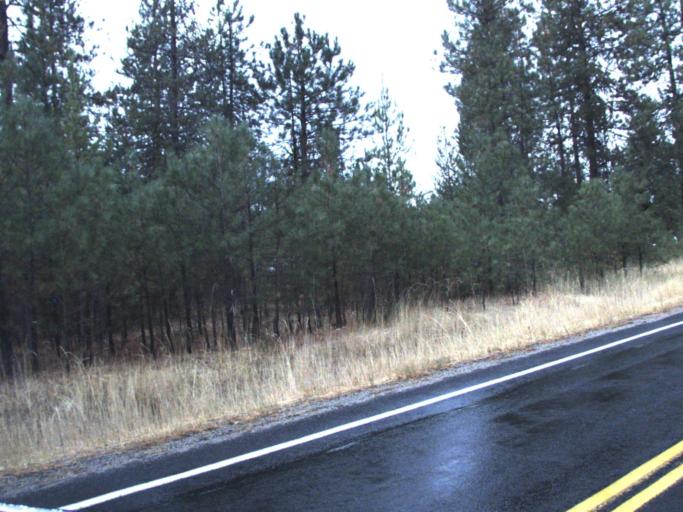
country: US
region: Washington
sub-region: Stevens County
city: Chewelah
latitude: 48.0168
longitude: -117.7312
